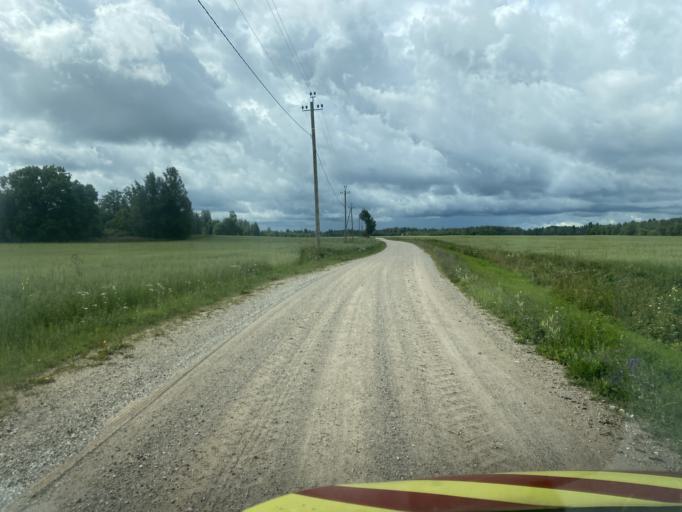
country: EE
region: Viljandimaa
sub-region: Karksi vald
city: Karksi-Nuia
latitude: 58.0741
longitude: 25.5202
